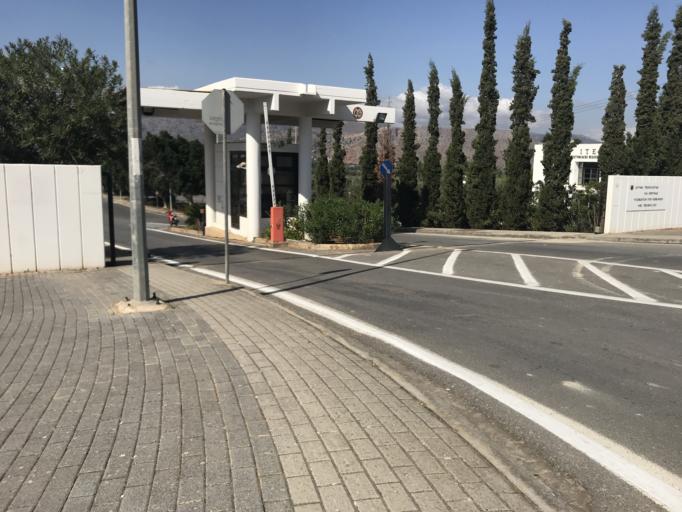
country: GR
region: Crete
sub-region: Nomos Irakleiou
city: Gazi
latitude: 35.3054
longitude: 25.0755
